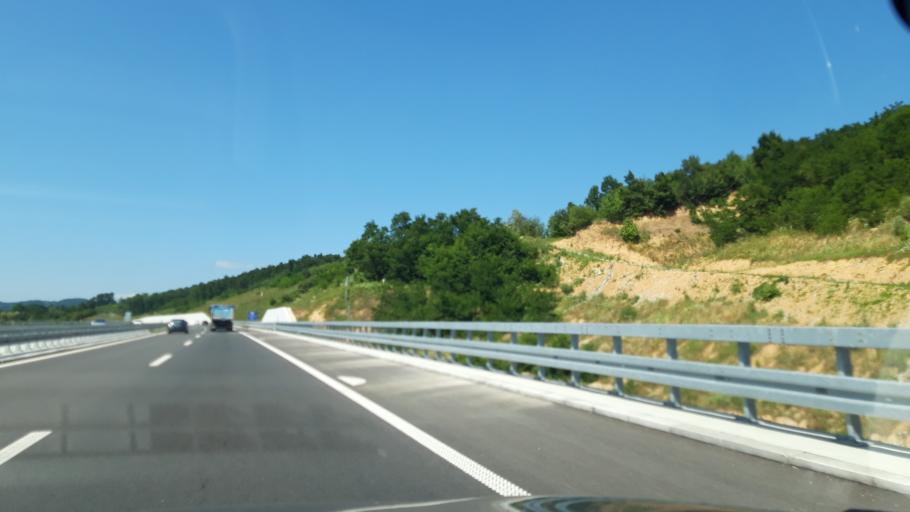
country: RS
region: Central Serbia
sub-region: Pcinjski Okrug
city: Vladicin Han
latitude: 42.6927
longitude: 22.0749
